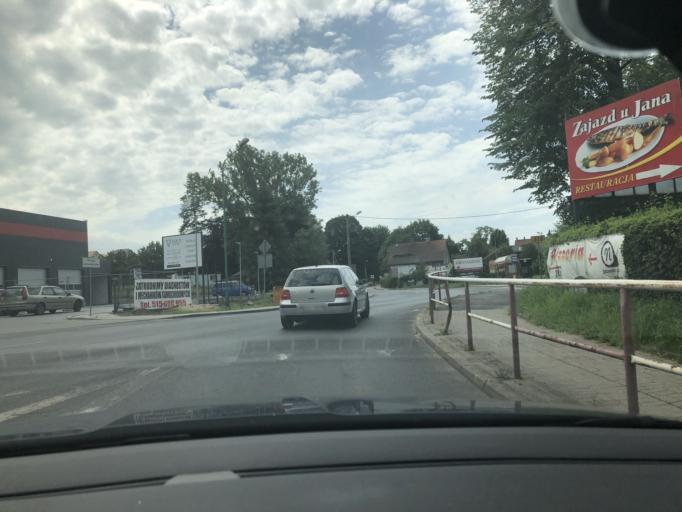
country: PL
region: Lower Silesian Voivodeship
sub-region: Powiat zlotoryjski
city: Zlotoryja
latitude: 51.1305
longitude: 15.9290
